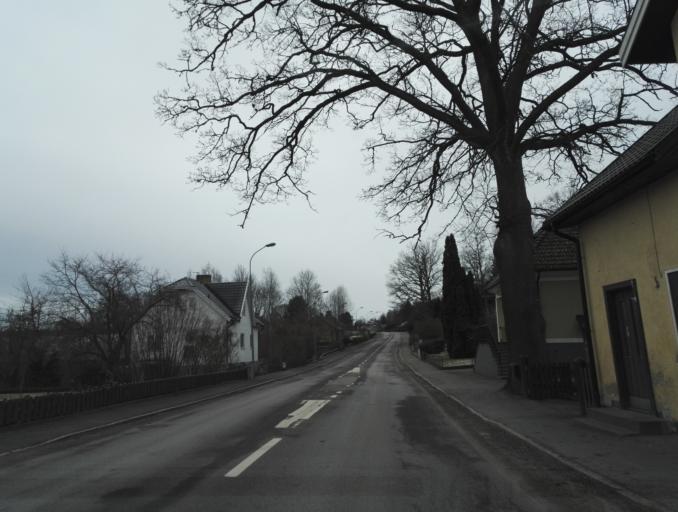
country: SE
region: Kalmar
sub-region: Hultsfreds Kommun
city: Virserum
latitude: 57.3145
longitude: 15.5851
